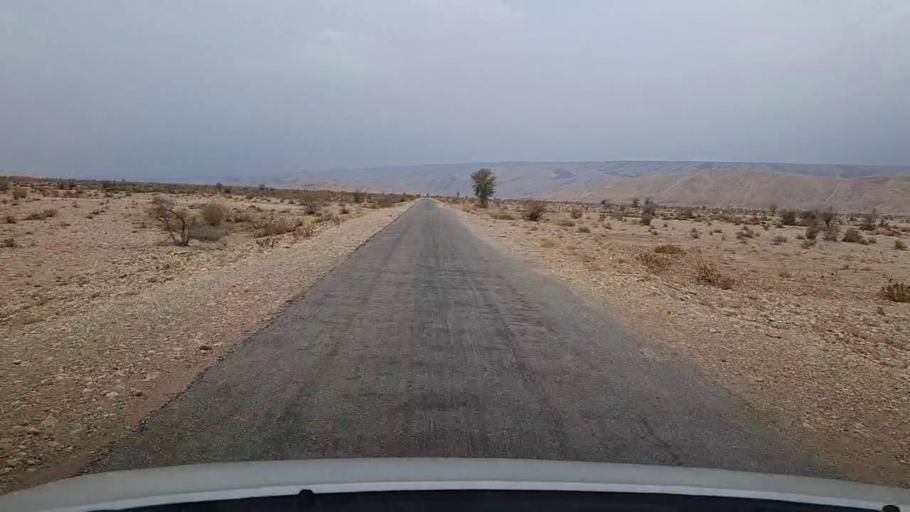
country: PK
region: Sindh
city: Sehwan
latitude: 26.2546
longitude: 67.7204
